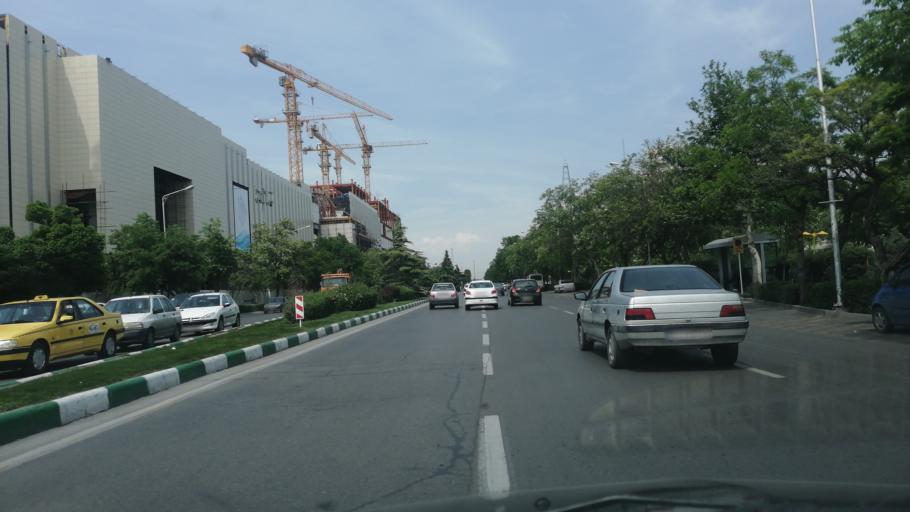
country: IR
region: Razavi Khorasan
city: Mashhad
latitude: 36.3151
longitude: 59.5606
